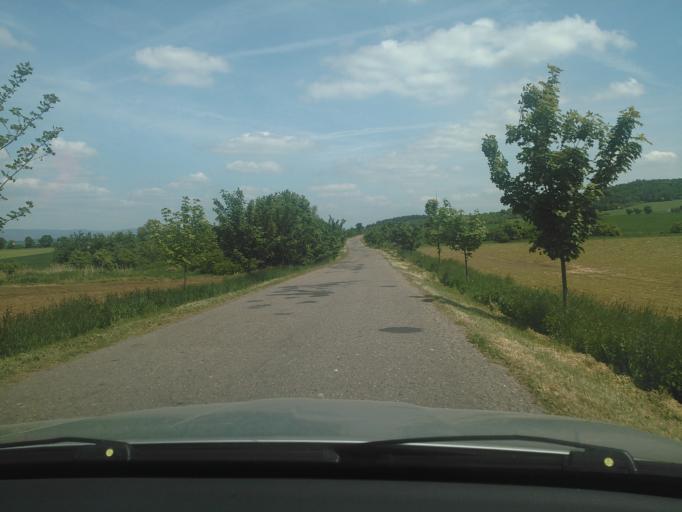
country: CZ
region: Ustecky
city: Becov
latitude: 50.4728
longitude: 13.7604
